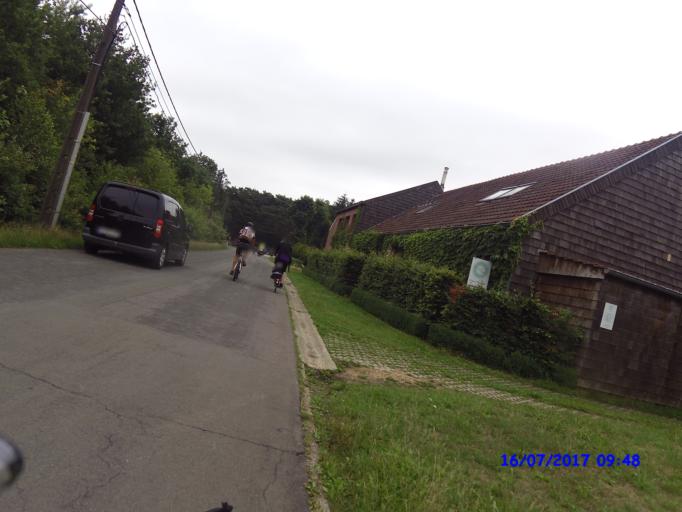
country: BE
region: Flanders
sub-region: Provincie Antwerpen
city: Herentals
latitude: 51.2101
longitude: 4.8584
